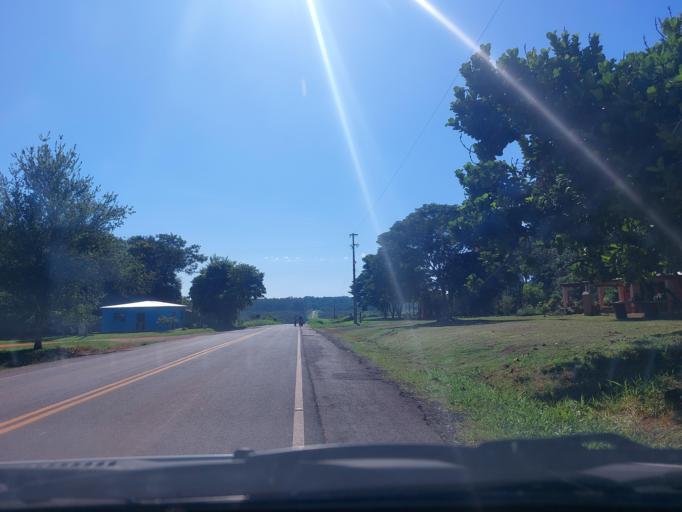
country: PY
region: San Pedro
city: Guayaybi
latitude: -24.3012
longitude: -56.1446
